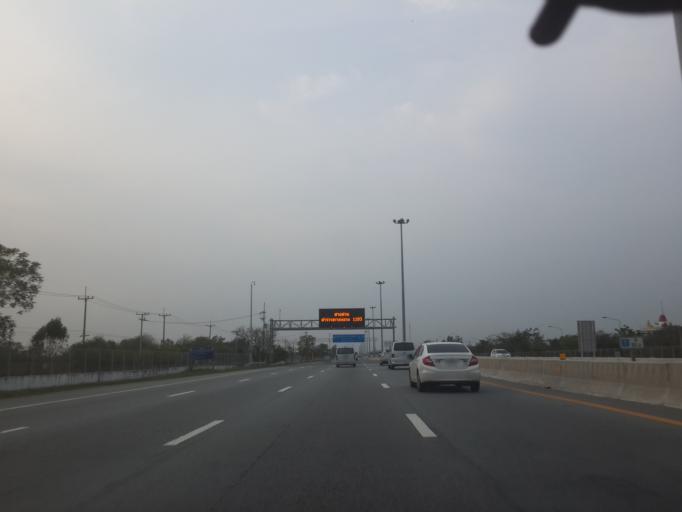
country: TH
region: Chachoengsao
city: Bang Pakong
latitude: 13.5260
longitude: 101.0200
